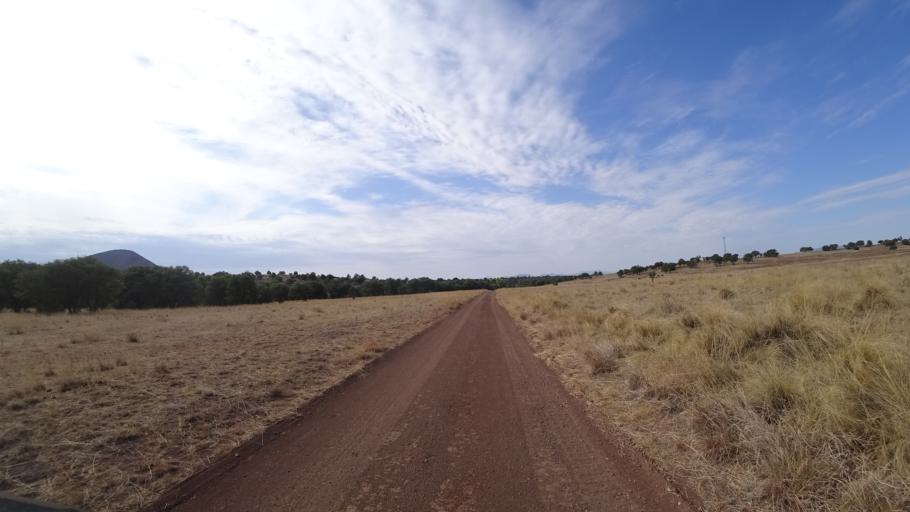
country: MX
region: Sonora
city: Santa Cruz
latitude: 31.4908
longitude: -110.5722
